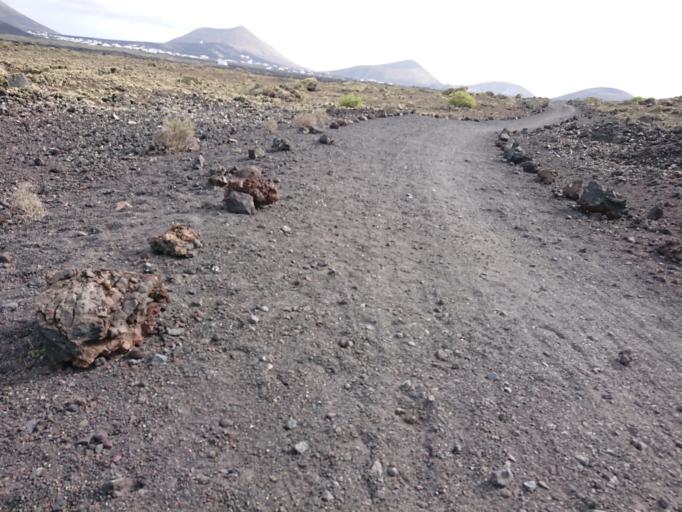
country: ES
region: Canary Islands
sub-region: Provincia de Las Palmas
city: Tinajo
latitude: 29.0082
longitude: -13.6759
